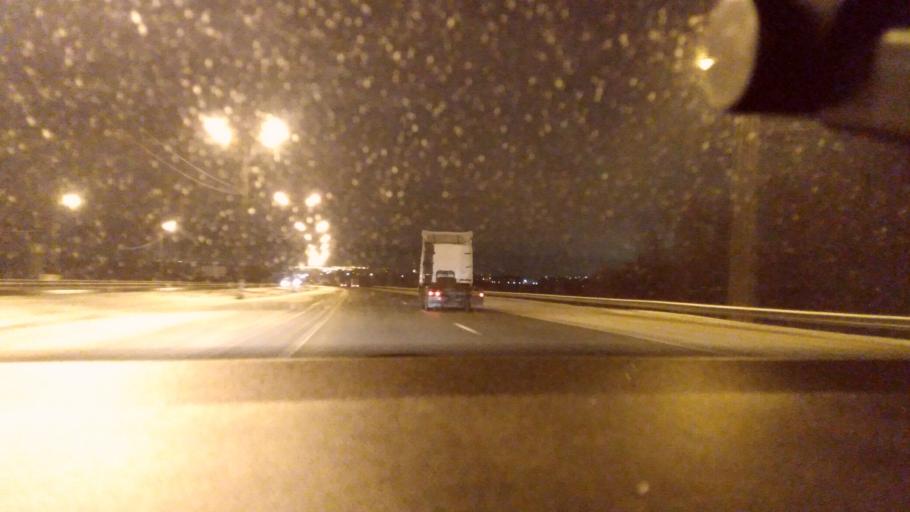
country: RU
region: Moskovskaya
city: Raduzhnyy
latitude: 55.1539
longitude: 38.6962
